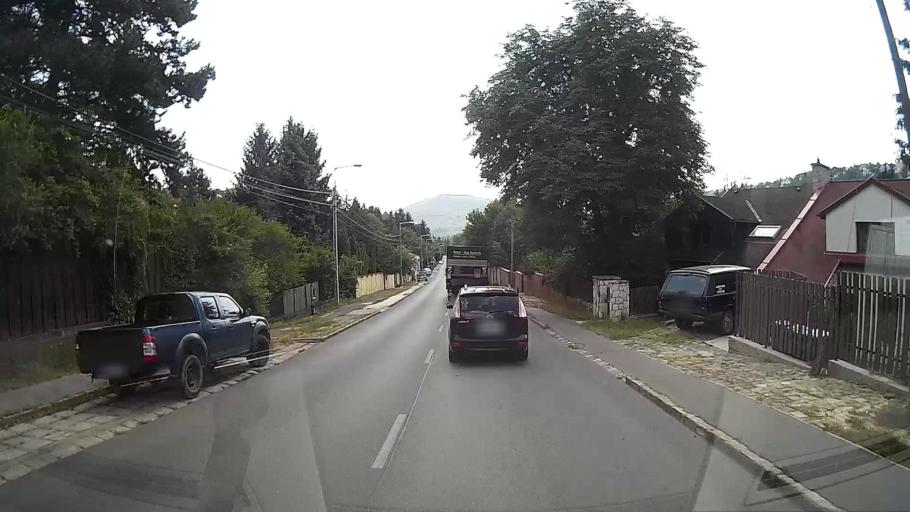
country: HU
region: Pest
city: Solymar
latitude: 47.5544
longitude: 18.9489
